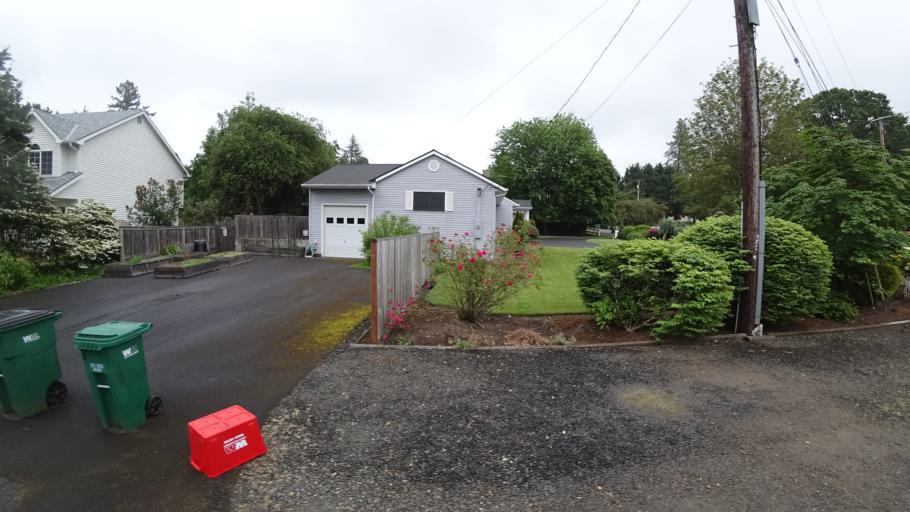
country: US
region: Oregon
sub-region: Washington County
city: Raleigh Hills
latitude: 45.4798
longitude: -122.7660
